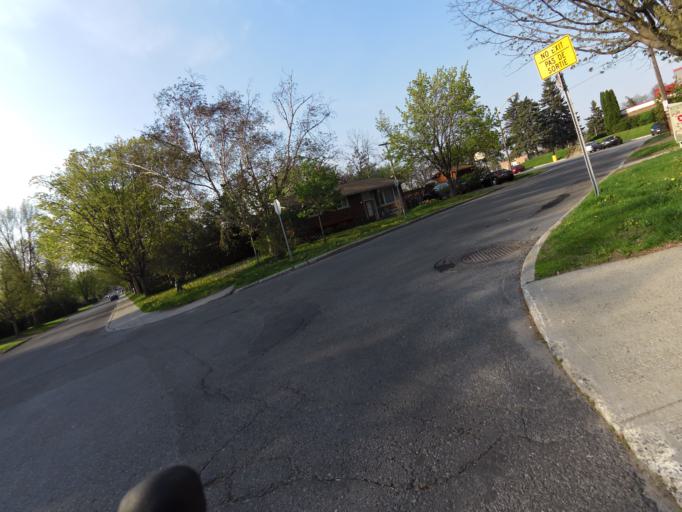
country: CA
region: Ontario
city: Bells Corners
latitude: 45.3473
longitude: -75.7752
